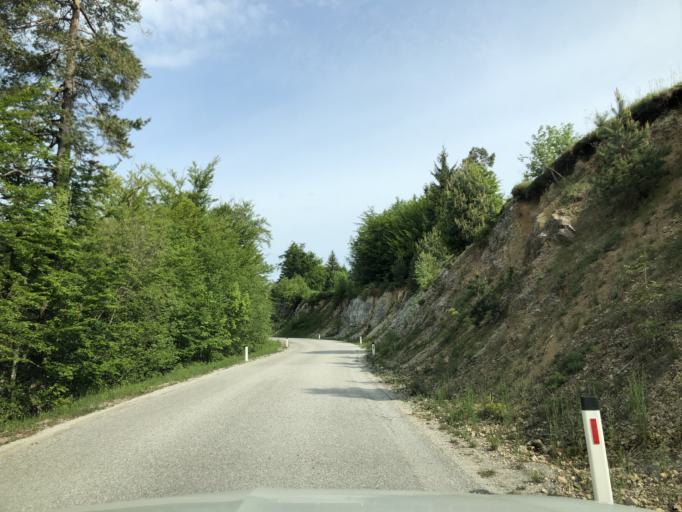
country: SI
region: Bloke
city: Nova Vas
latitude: 45.7994
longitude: 14.5532
